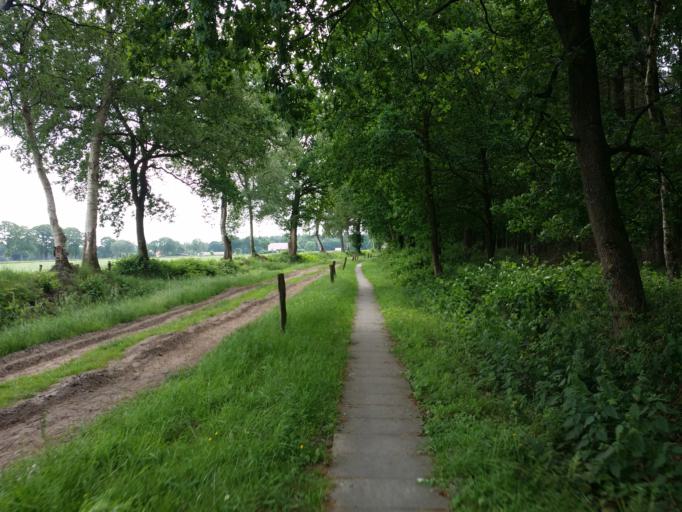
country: DE
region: Lower Saxony
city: Friedeburg
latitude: 53.5019
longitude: 7.8114
